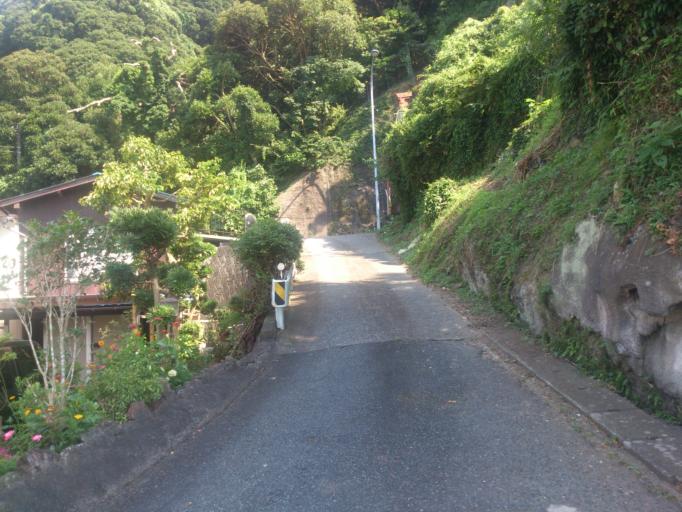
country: JP
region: Chiba
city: Tateyama
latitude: 35.0771
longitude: 139.8376
